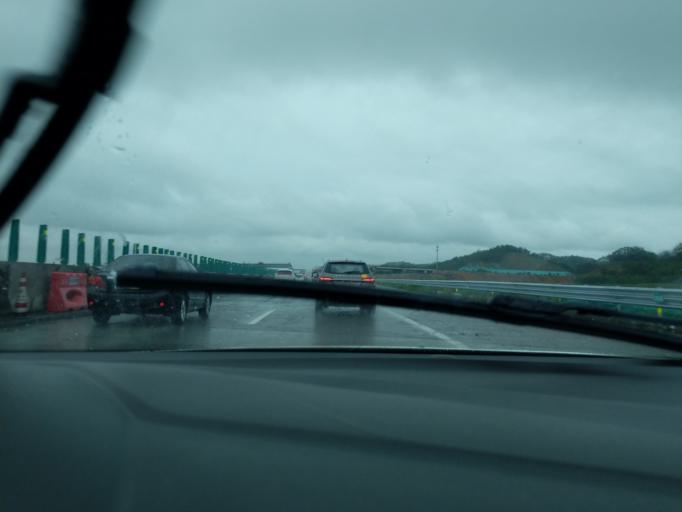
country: CN
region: Guangdong
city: Yueshan
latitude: 22.4647
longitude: 112.7075
